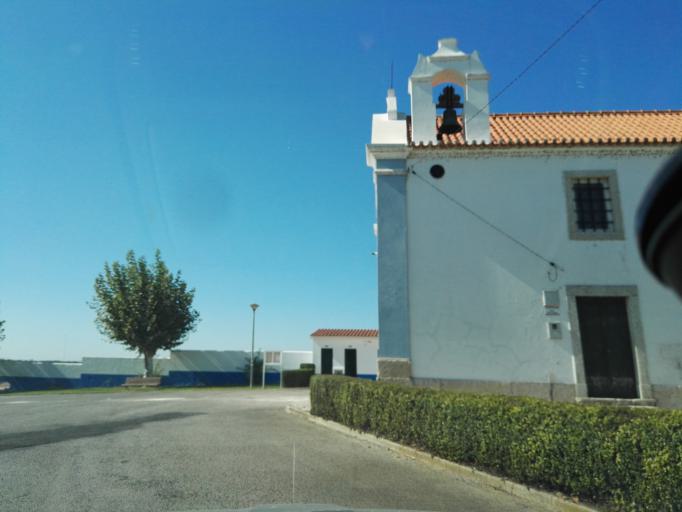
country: PT
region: Santarem
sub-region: Benavente
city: Poceirao
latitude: 38.8658
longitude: -8.7512
